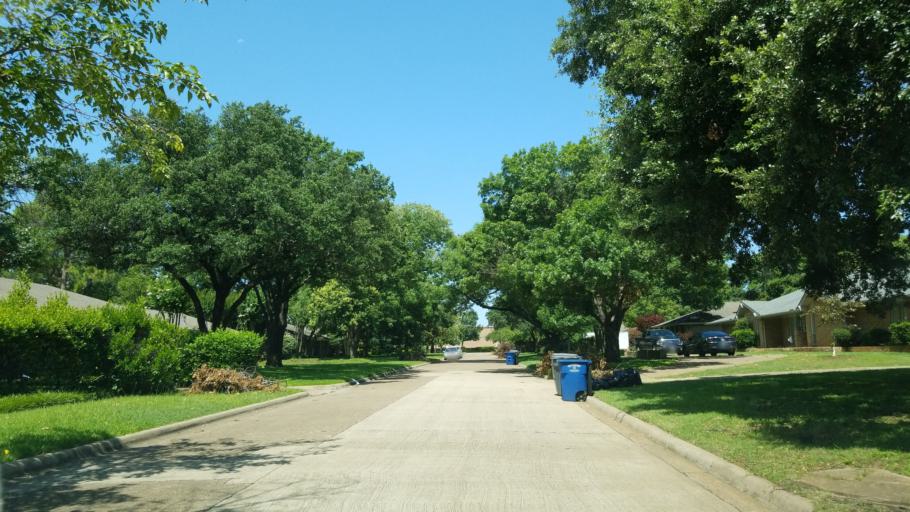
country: US
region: Texas
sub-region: Dallas County
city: Farmers Branch
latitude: 32.9090
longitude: -96.8495
